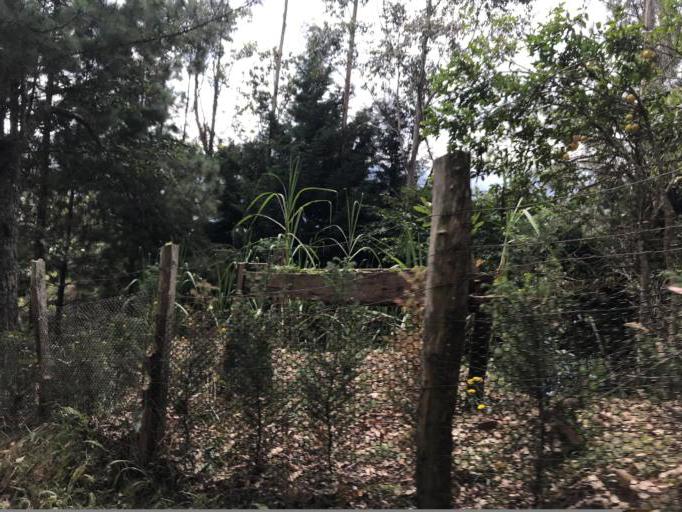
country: CO
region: Valle del Cauca
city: Cali
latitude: 3.4632
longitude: -76.6495
